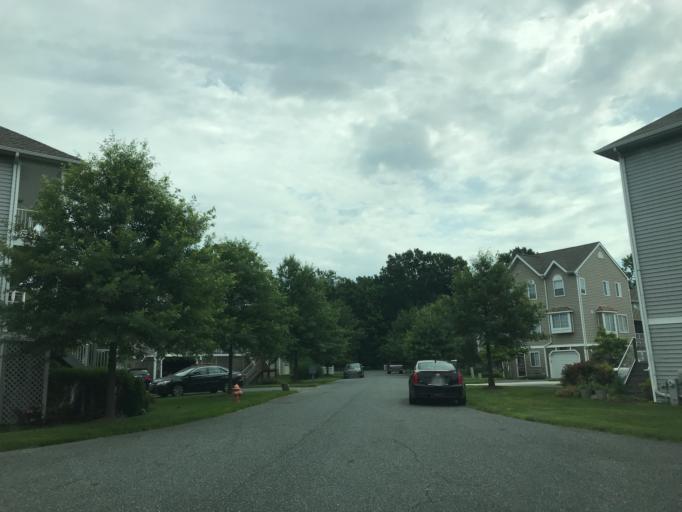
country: US
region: Maryland
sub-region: Baltimore County
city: Bowleys Quarters
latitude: 39.3342
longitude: -76.4085
